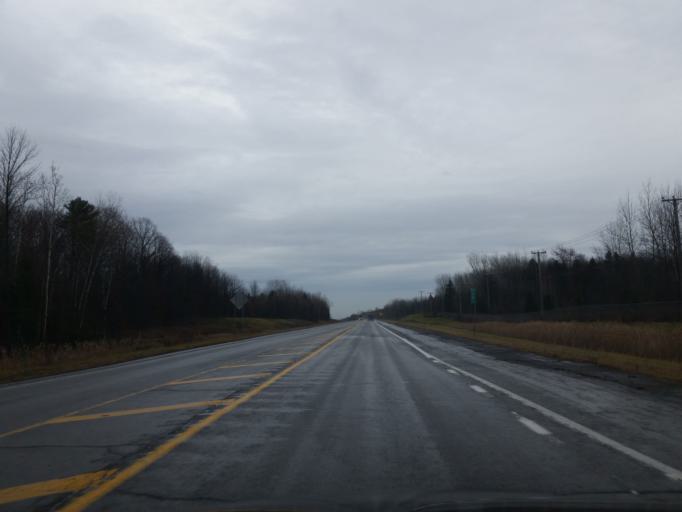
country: CA
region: Quebec
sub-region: Laurentides
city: Mirabel
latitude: 45.6837
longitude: -74.0750
